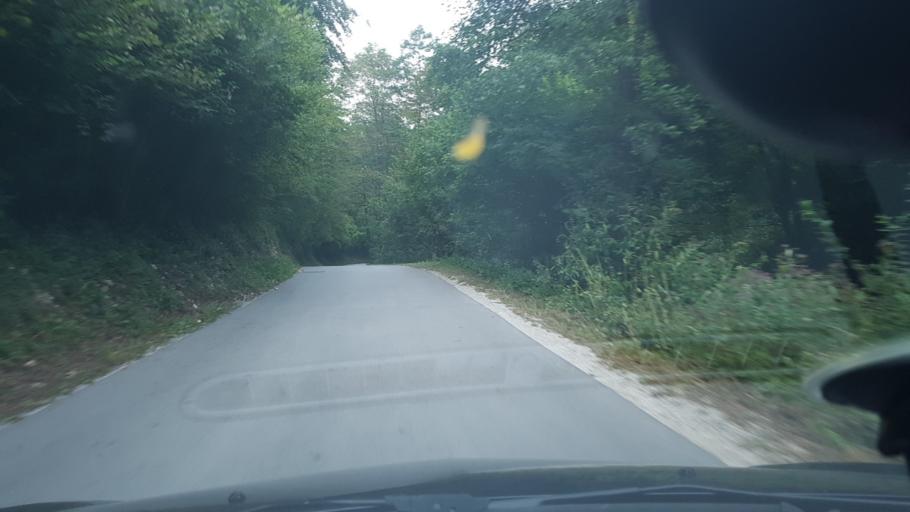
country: SI
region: Krsko
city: Senovo
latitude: 46.0154
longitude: 15.4892
